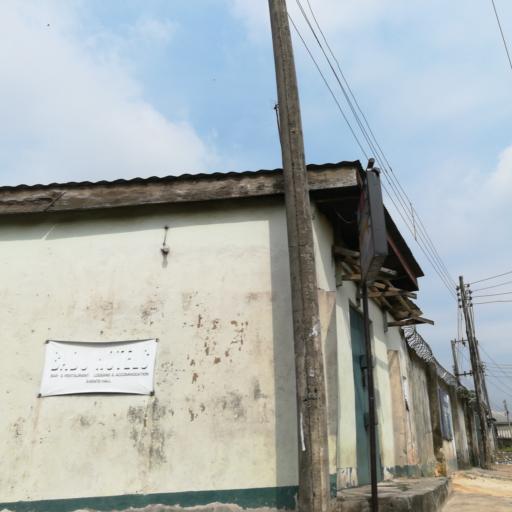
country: NG
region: Rivers
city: Port Harcourt
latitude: 4.8356
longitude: 7.0669
